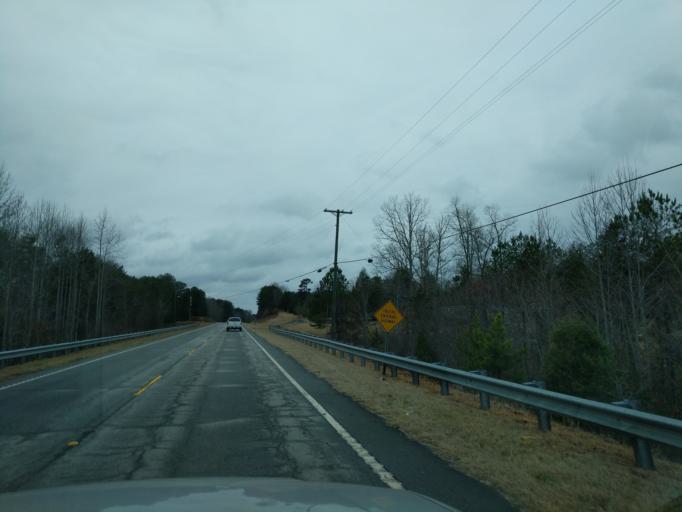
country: US
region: South Carolina
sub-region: Oconee County
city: Walhalla
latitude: 34.9124
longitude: -82.9418
